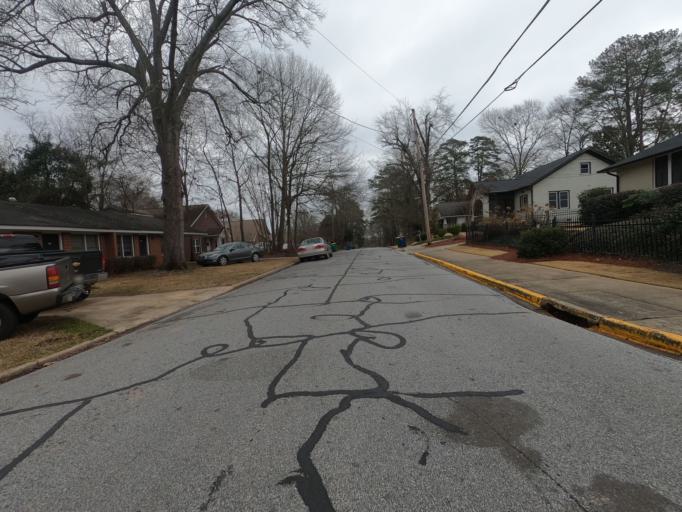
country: US
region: Georgia
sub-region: Clarke County
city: Athens
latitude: 33.9385
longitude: -83.3793
